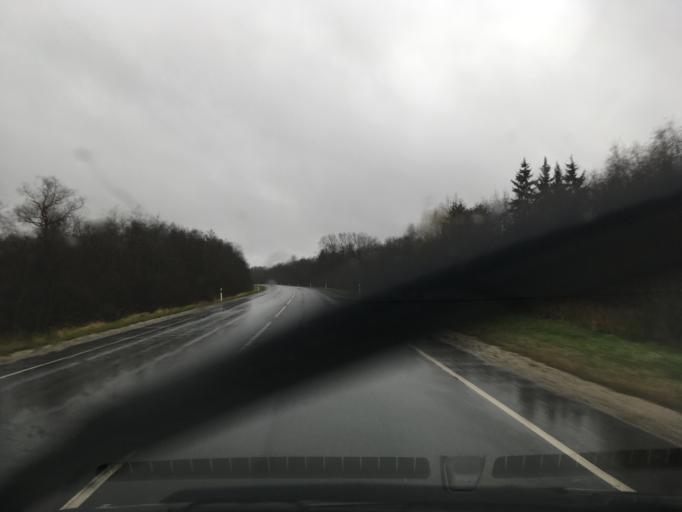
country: EE
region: Laeaene
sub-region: Lihula vald
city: Lihula
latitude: 58.8321
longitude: 24.0546
